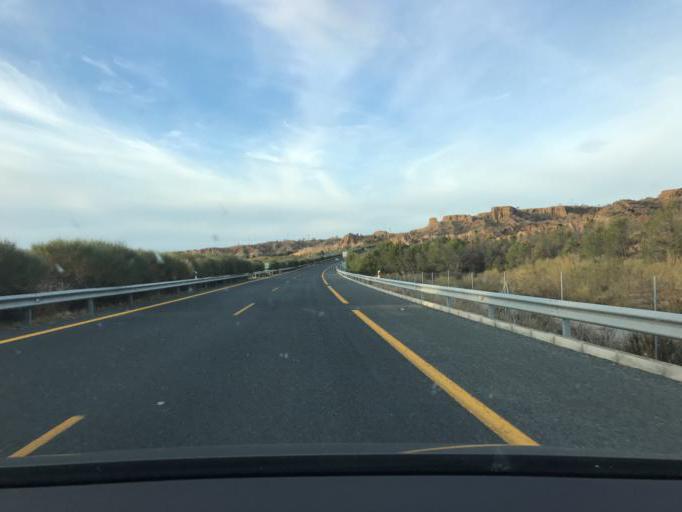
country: ES
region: Andalusia
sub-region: Provincia de Granada
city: Guadix
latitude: 37.3047
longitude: -3.1114
